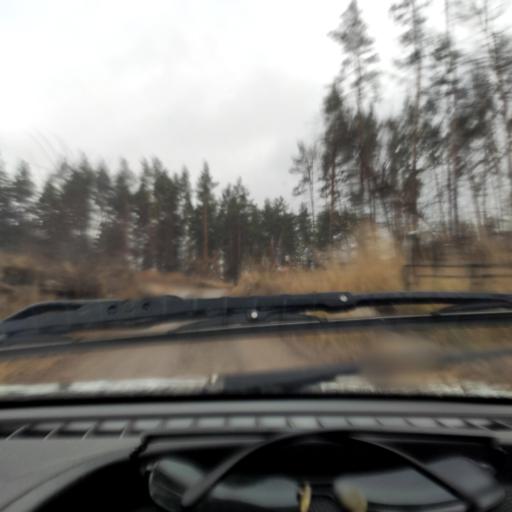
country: RU
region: Samara
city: Zhigulevsk
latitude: 53.5351
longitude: 49.5549
